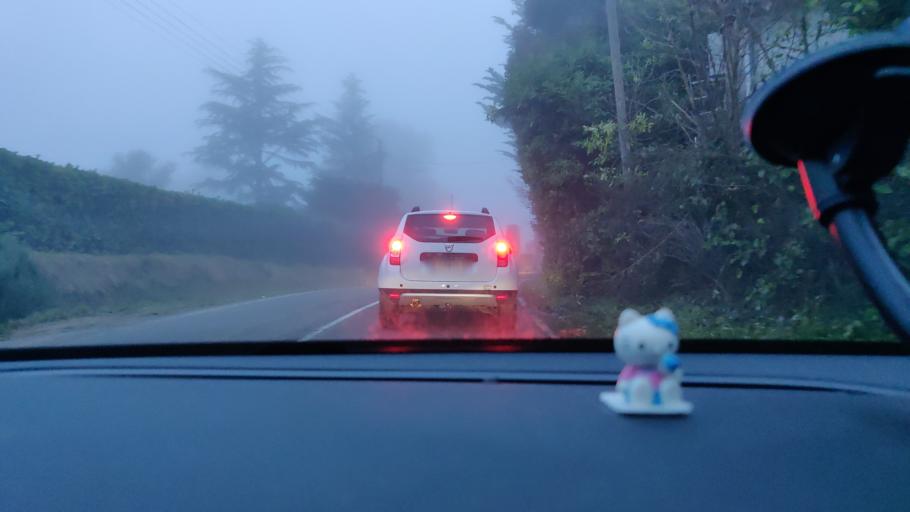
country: FR
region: Midi-Pyrenees
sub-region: Departement de la Haute-Garonne
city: Vieille-Toulouse
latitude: 43.5151
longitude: 1.4623
